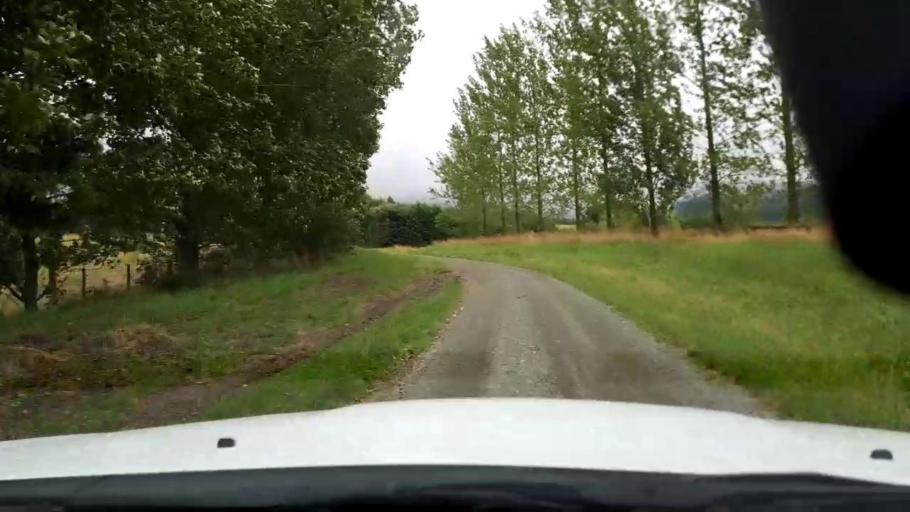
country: NZ
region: Canterbury
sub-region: Timaru District
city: Pleasant Point
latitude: -44.1029
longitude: 171.1341
